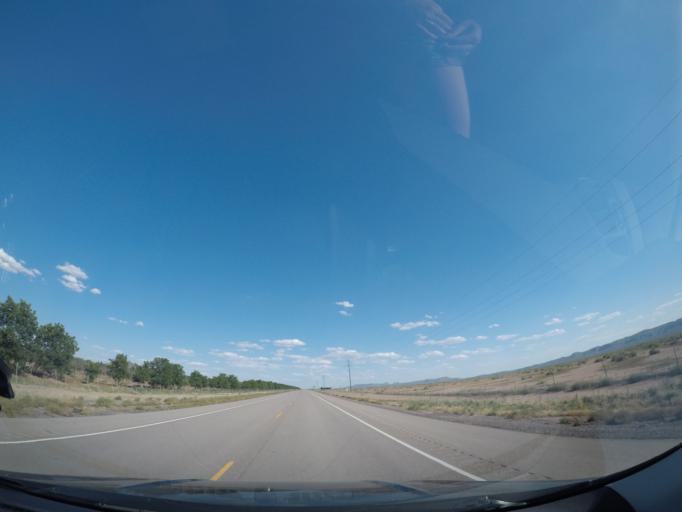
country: US
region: Texas
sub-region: Culberson County
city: Van Horn
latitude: 30.8316
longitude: -104.7618
